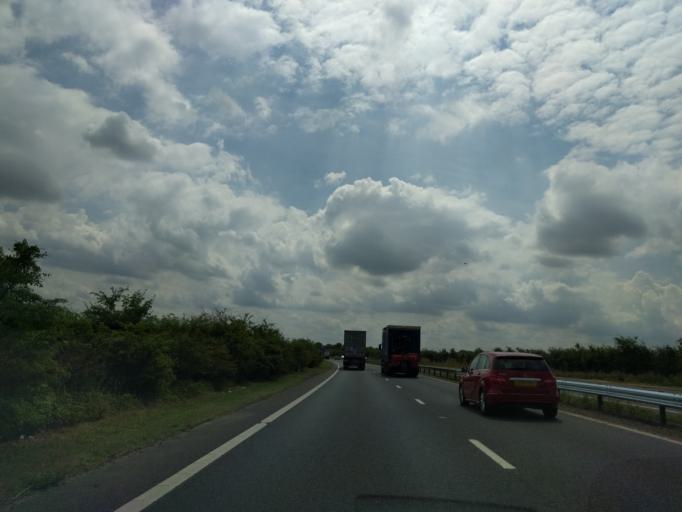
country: GB
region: England
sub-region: Cambridgeshire
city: Waterbeach
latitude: 52.2202
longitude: 0.1889
